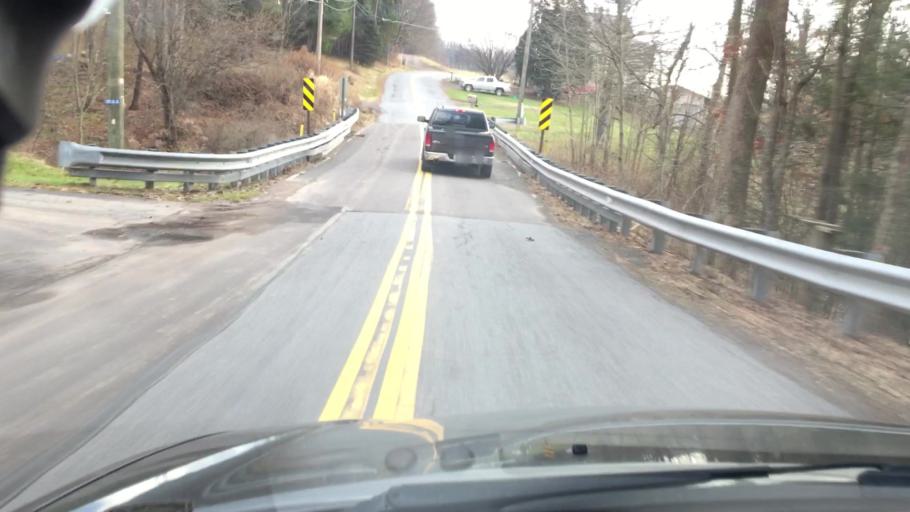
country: US
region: Pennsylvania
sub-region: Luzerne County
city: Back Mountain
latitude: 41.3239
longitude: -76.0671
